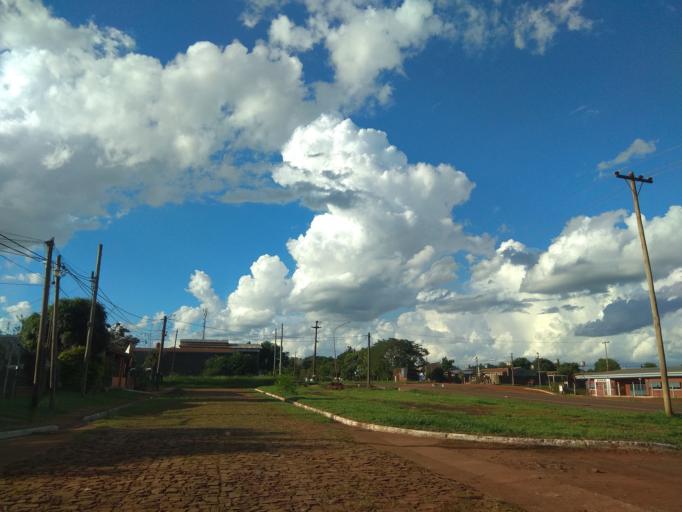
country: AR
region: Misiones
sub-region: Departamento de Candelaria
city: Candelaria
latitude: -27.4797
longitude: -55.7472
